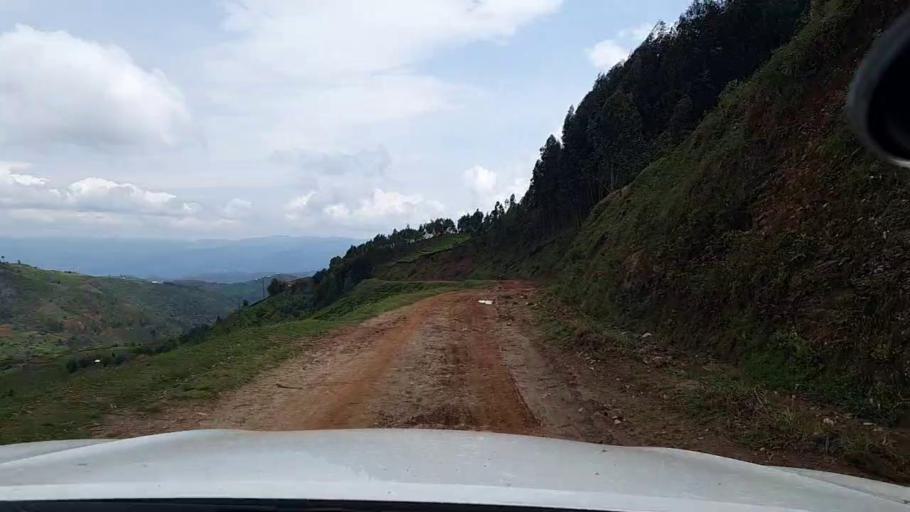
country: RW
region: Western Province
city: Kibuye
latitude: -2.1671
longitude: 29.3988
